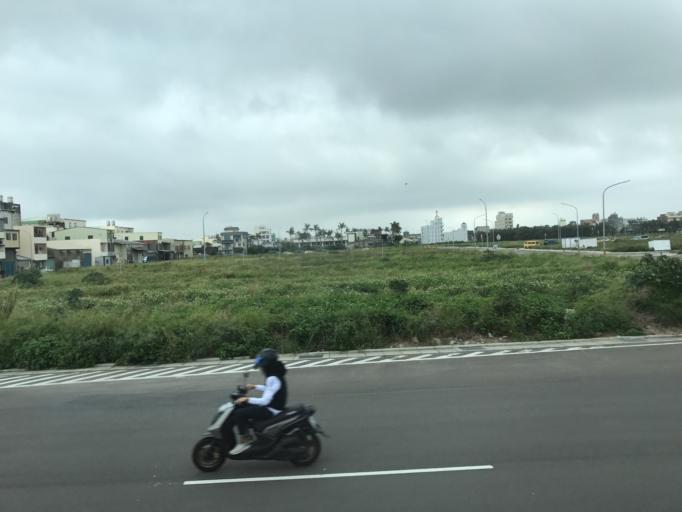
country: TW
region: Taiwan
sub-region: Hsinchu
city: Hsinchu
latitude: 24.8208
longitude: 120.9527
